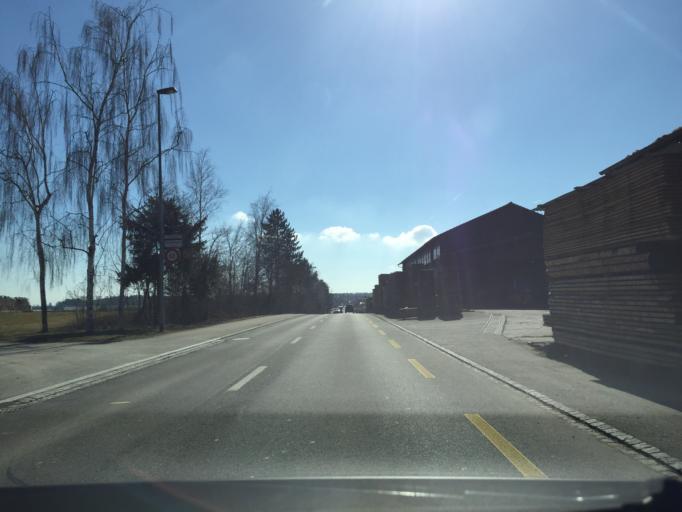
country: CH
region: Thurgau
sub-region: Frauenfeld District
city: Diessenhofen
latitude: 47.6832
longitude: 8.7502
